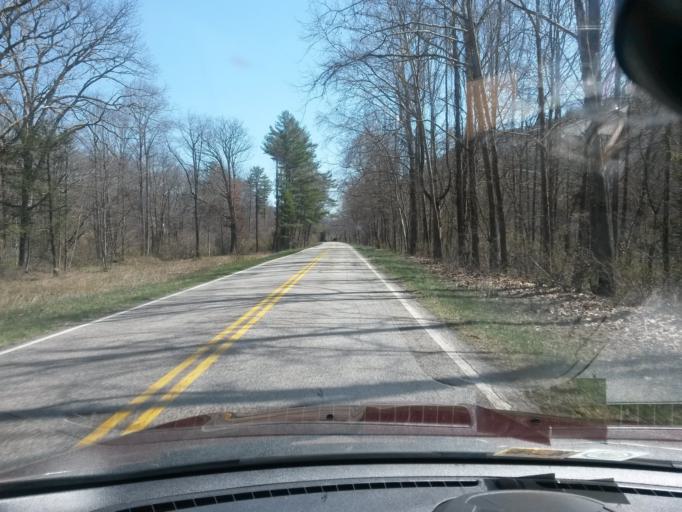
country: US
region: Virginia
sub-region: City of Covington
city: Covington
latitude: 37.8153
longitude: -80.0980
